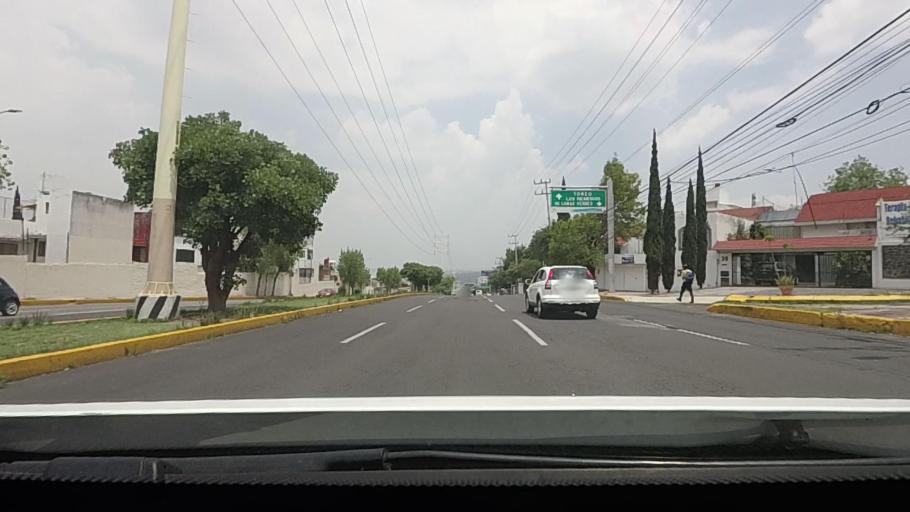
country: MX
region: Mexico
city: Naucalpan de Juarez
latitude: 19.5027
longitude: -99.2506
